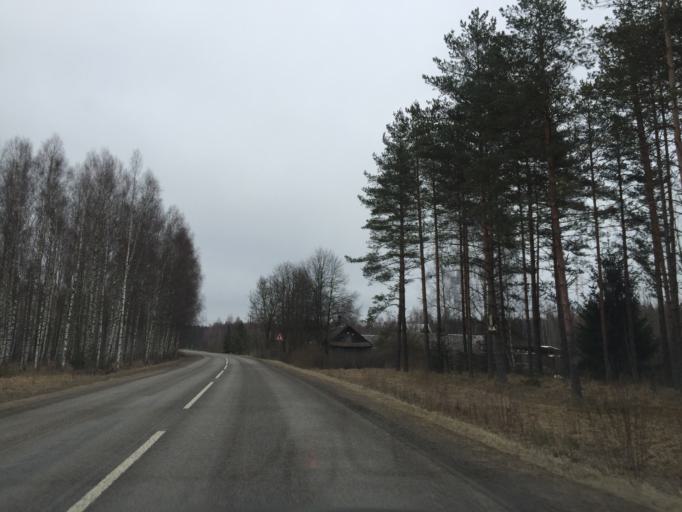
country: LV
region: Garkalne
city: Garkalne
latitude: 56.9521
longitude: 24.4353
